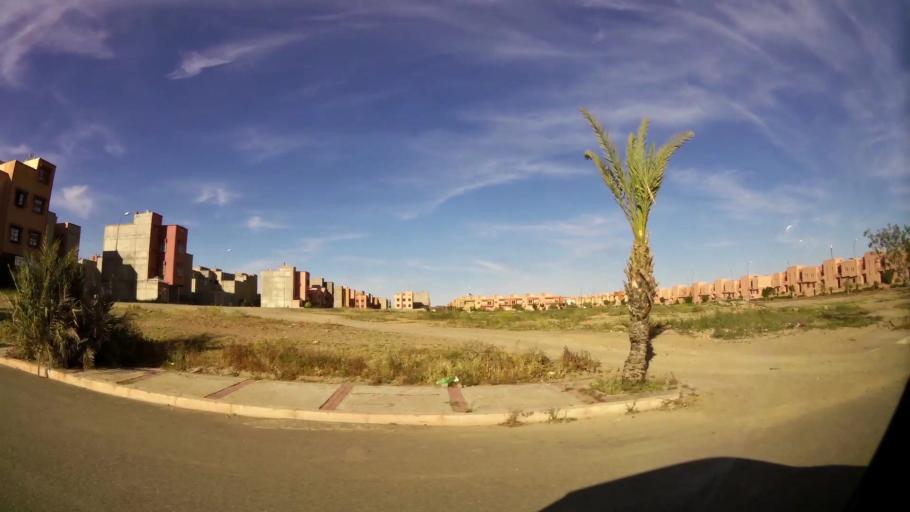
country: MA
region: Marrakech-Tensift-Al Haouz
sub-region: Marrakech
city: Marrakesh
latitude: 31.7504
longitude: -8.1046
